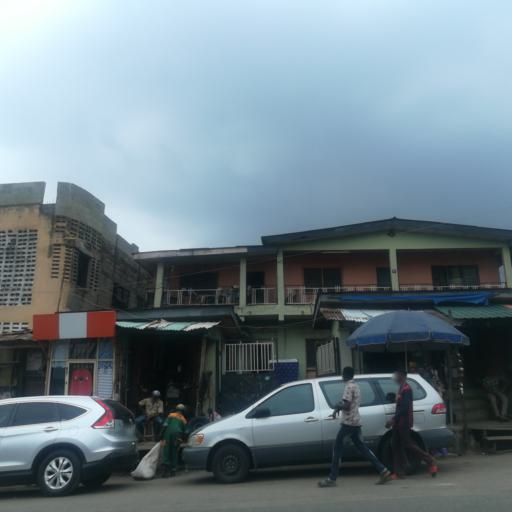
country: NG
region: Lagos
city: Ojota
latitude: 6.5871
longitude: 3.3827
